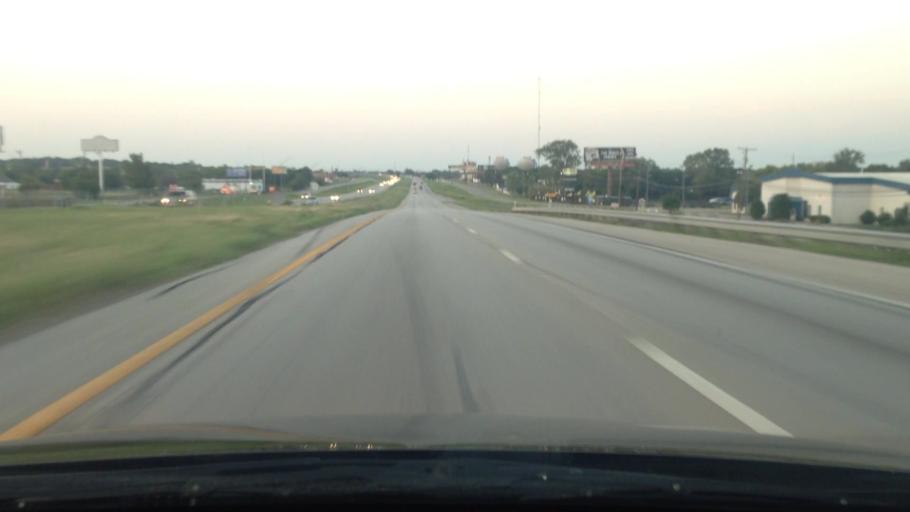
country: US
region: Texas
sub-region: Tarrant County
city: Forest Hill
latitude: 32.7085
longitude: -97.2311
